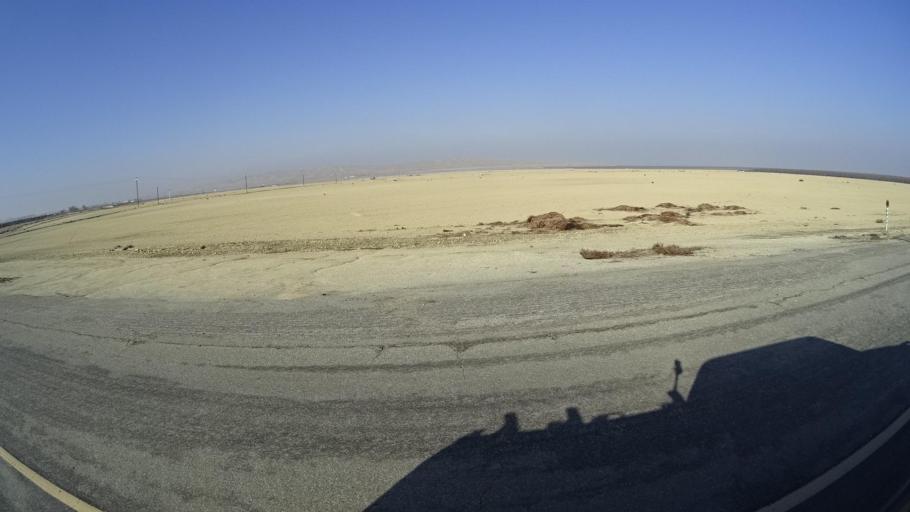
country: US
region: California
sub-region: Kern County
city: Maricopa
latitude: 35.1015
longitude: -119.3661
